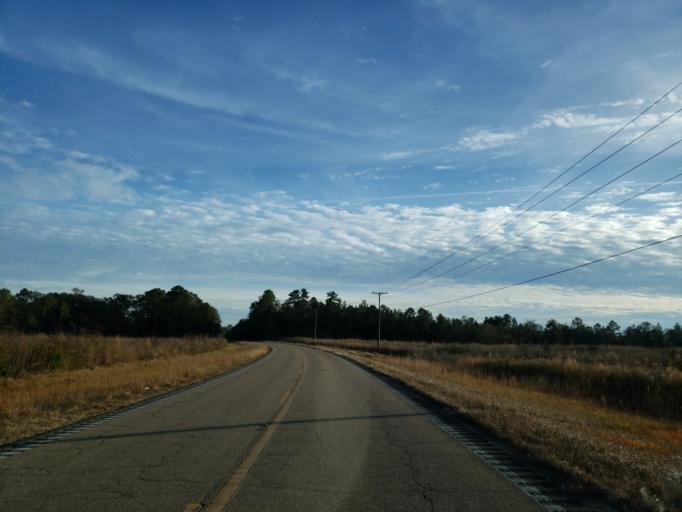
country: US
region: Mississippi
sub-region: Lamar County
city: West Hattiesburg
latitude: 31.2686
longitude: -89.4663
